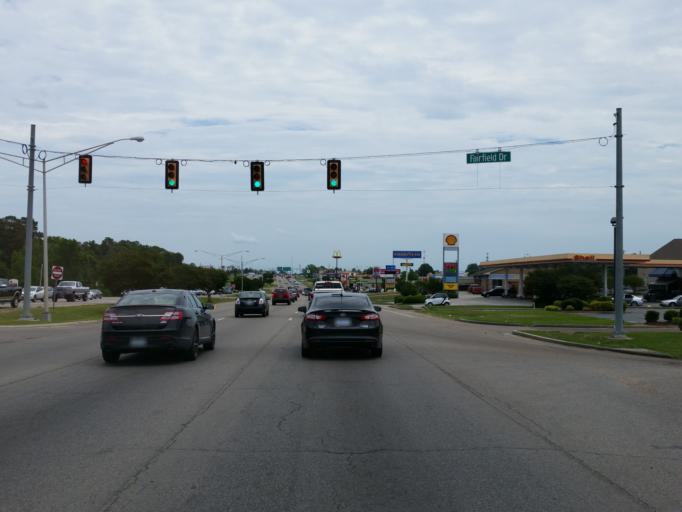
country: US
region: Mississippi
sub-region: Lamar County
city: West Hattiesburg
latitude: 31.3227
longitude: -89.3678
